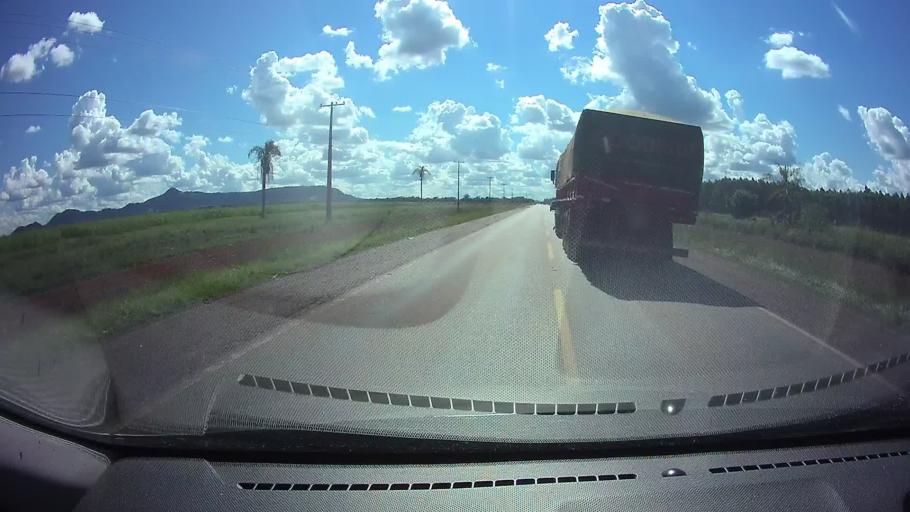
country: PY
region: Guaira
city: Coronel Martinez
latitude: -25.7613
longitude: -56.7433
